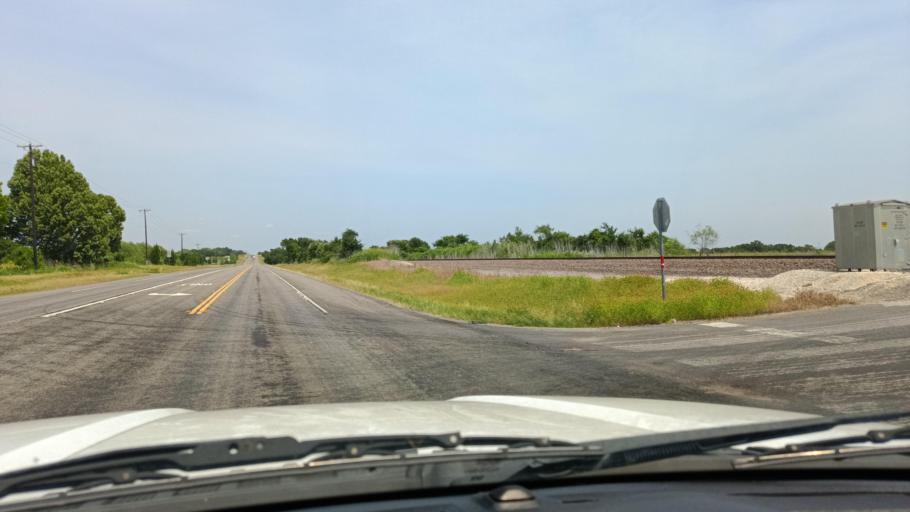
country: US
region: Texas
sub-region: Milam County
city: Cameron
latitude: 30.8488
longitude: -97.0698
